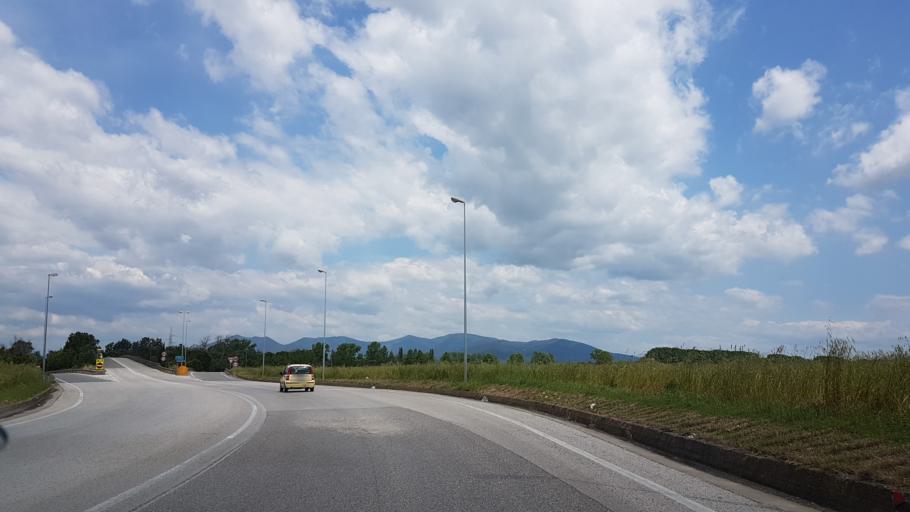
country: IT
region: Tuscany
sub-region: Provincia di Livorno
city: Vicarello
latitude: 43.6204
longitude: 10.4663
